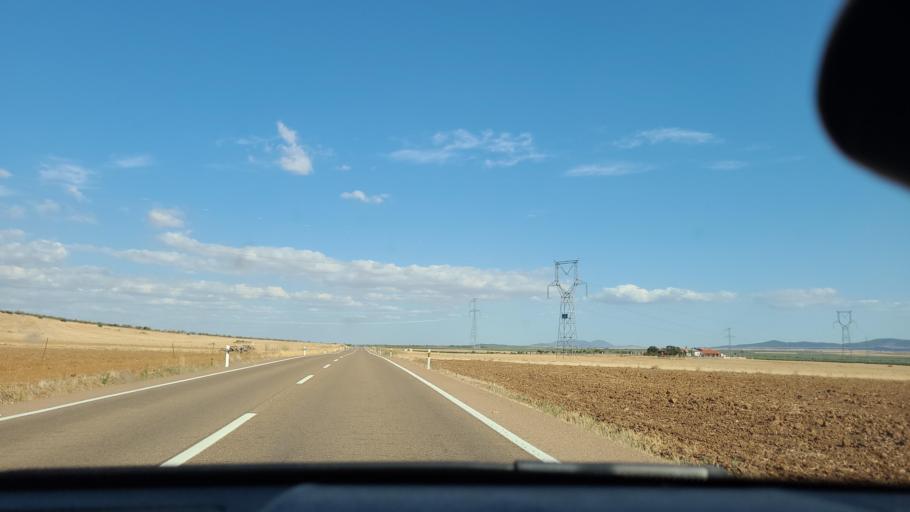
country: ES
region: Extremadura
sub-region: Provincia de Badajoz
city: Usagre
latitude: 38.3583
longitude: -6.2132
